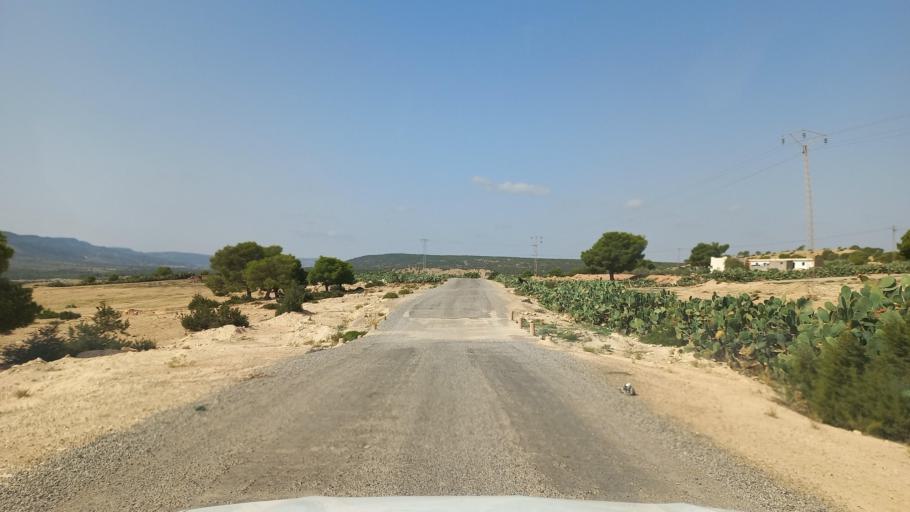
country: TN
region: Al Qasrayn
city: Sbiba
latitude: 35.3986
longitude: 8.9591
